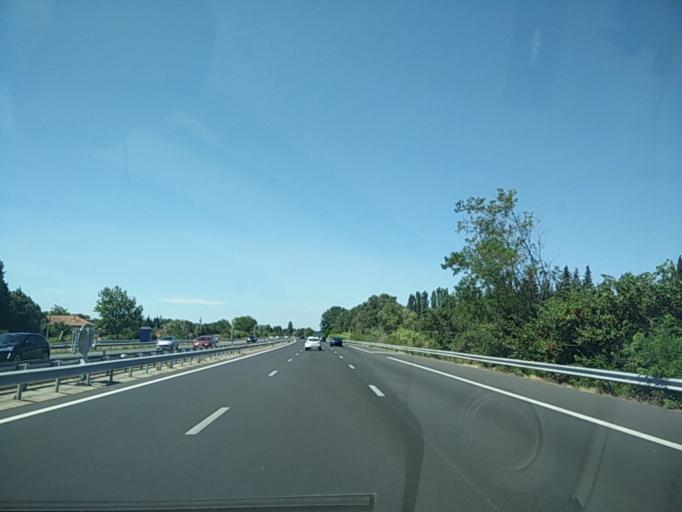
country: FR
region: Provence-Alpes-Cote d'Azur
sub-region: Departement du Vaucluse
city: Caumont-sur-Durance
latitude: 43.8770
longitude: 4.9397
